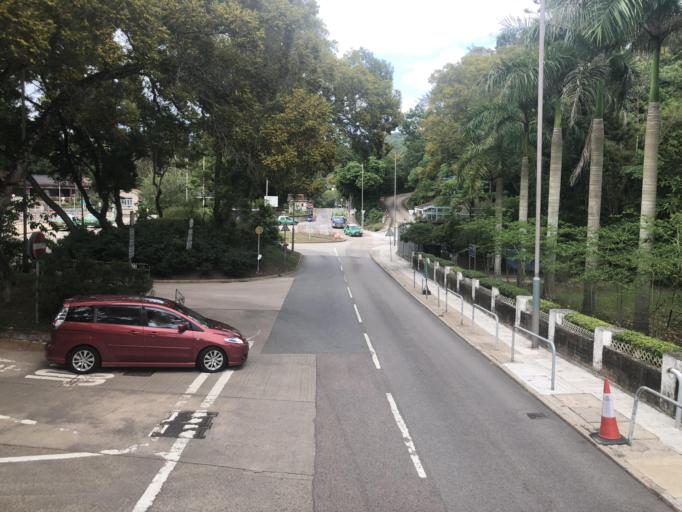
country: HK
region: Sai Kung
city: Sai Kung
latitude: 22.3966
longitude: 114.3190
